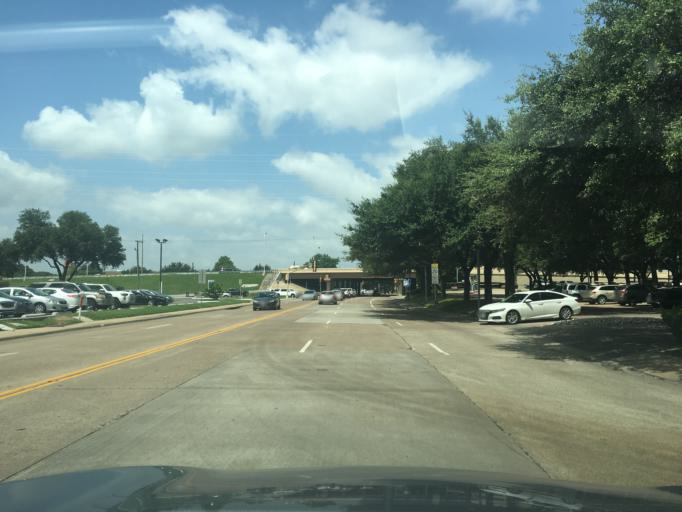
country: US
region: Texas
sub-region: Dallas County
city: Addison
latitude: 32.9220
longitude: -96.8168
